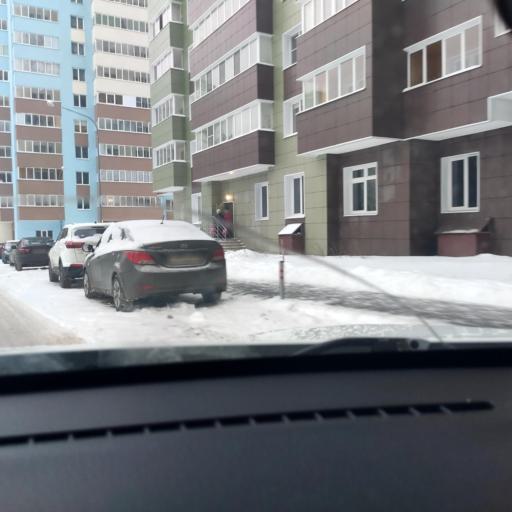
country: RU
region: Tatarstan
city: Osinovo
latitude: 55.8662
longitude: 48.8741
